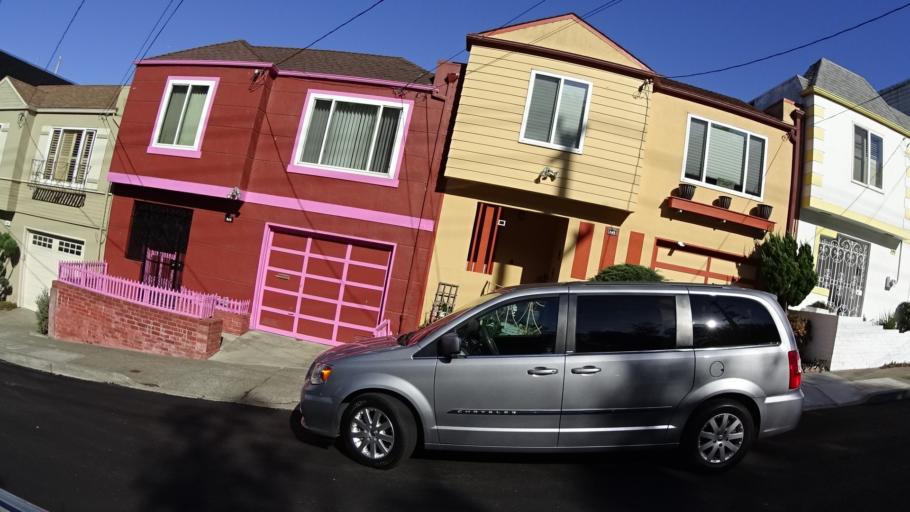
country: US
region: California
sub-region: San Mateo County
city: Brisbane
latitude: 37.7198
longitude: -122.4113
